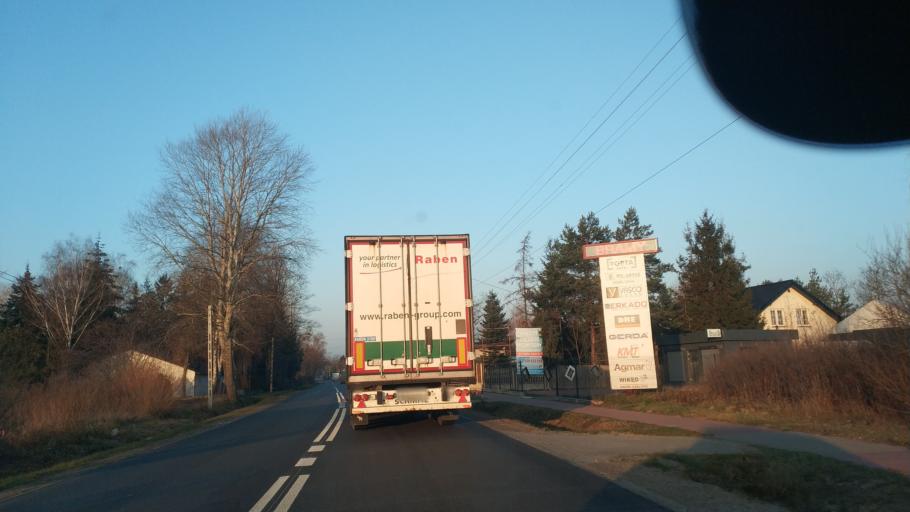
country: PL
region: Masovian Voivodeship
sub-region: Powiat pruszkowski
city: Owczarnia
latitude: 52.0869
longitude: 20.6849
